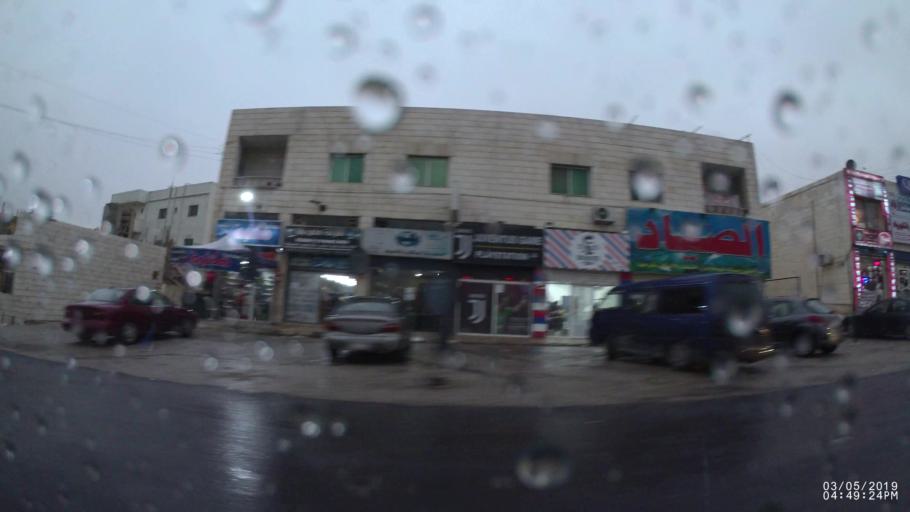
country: JO
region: Amman
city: Amman
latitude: 32.0022
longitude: 35.9629
